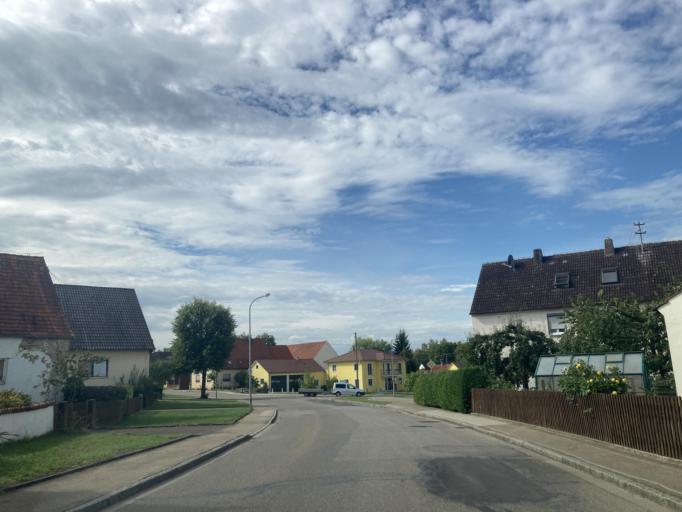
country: DE
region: Bavaria
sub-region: Swabia
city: Alerheim
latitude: 48.8437
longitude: 10.6238
